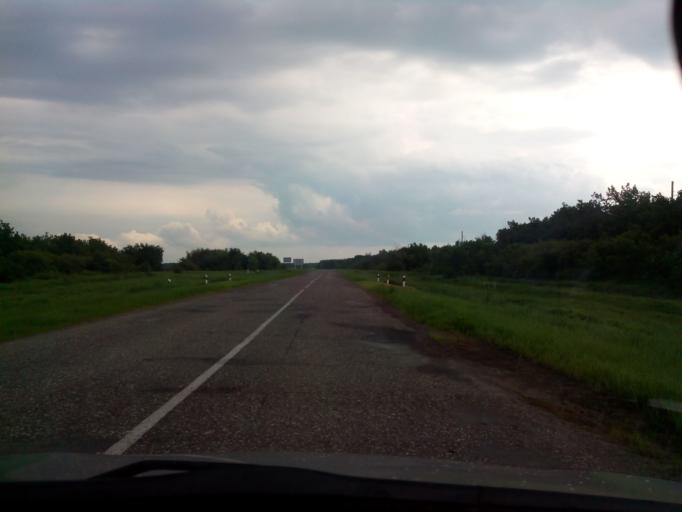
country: RU
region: Volgograd
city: Kumylzhenskaya
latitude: 49.8981
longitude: 42.8276
